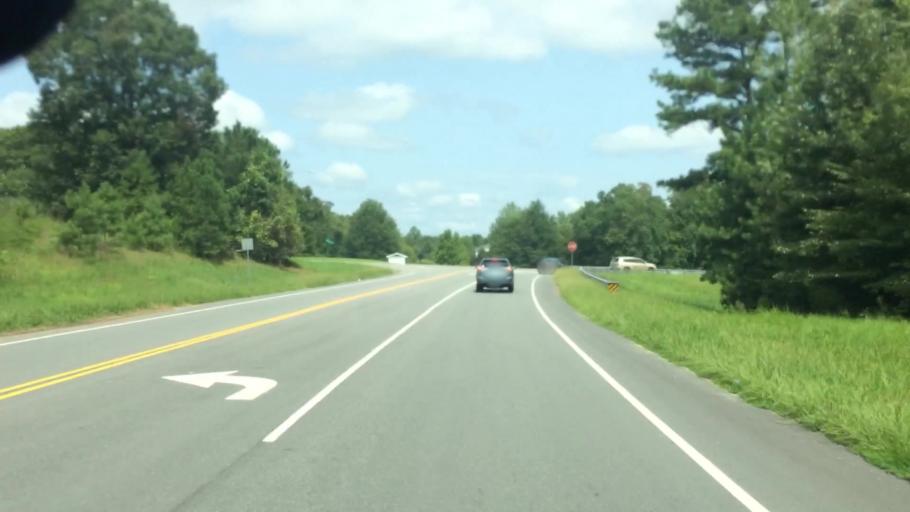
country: US
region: Virginia
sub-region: James City County
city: Williamsburg
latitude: 37.2623
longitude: -76.7885
